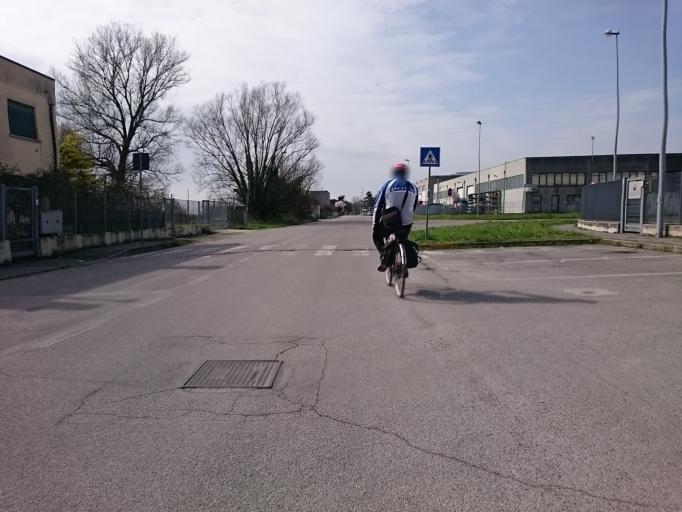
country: IT
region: Veneto
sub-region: Provincia di Padova
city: Terradura
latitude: 45.3435
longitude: 11.8329
